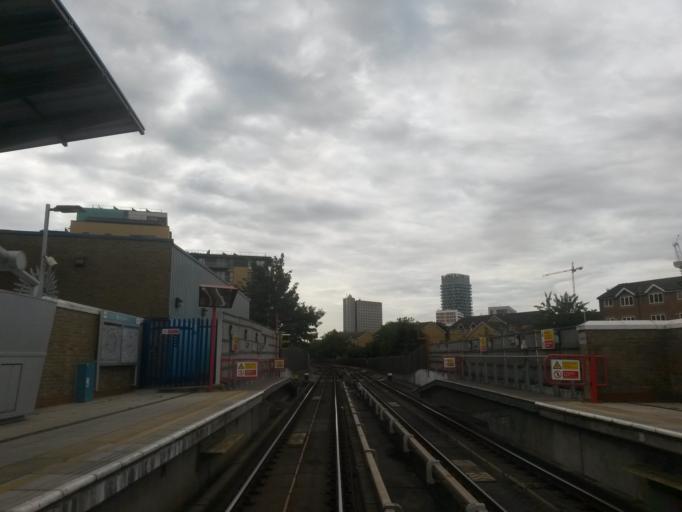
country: GB
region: England
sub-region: Greater London
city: Catford
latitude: 51.4685
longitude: -0.0161
